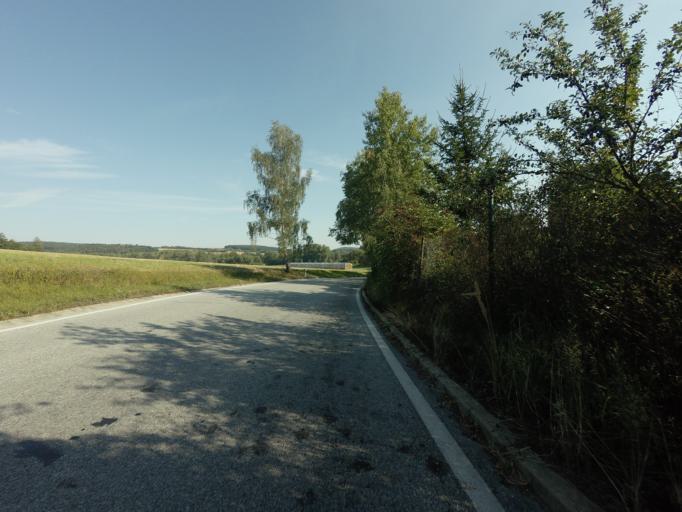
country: CZ
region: Jihocesky
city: Tyn nad Vltavou
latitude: 49.2415
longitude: 14.4200
